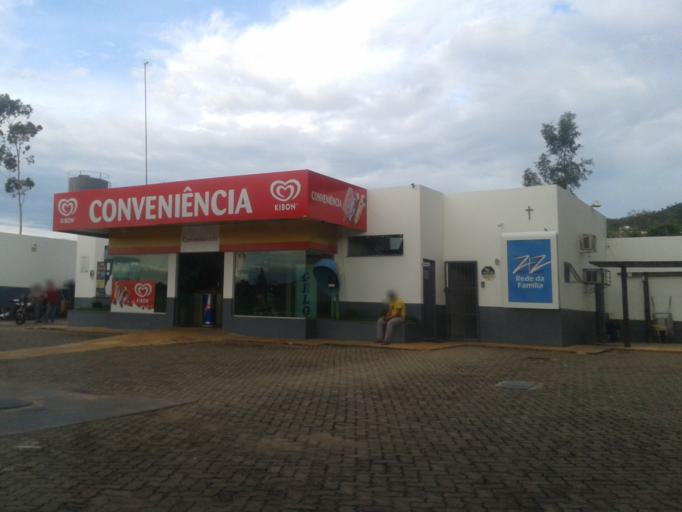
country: BR
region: Goias
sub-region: Caldas Novas
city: Caldas Novas
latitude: -17.7649
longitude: -48.7543
